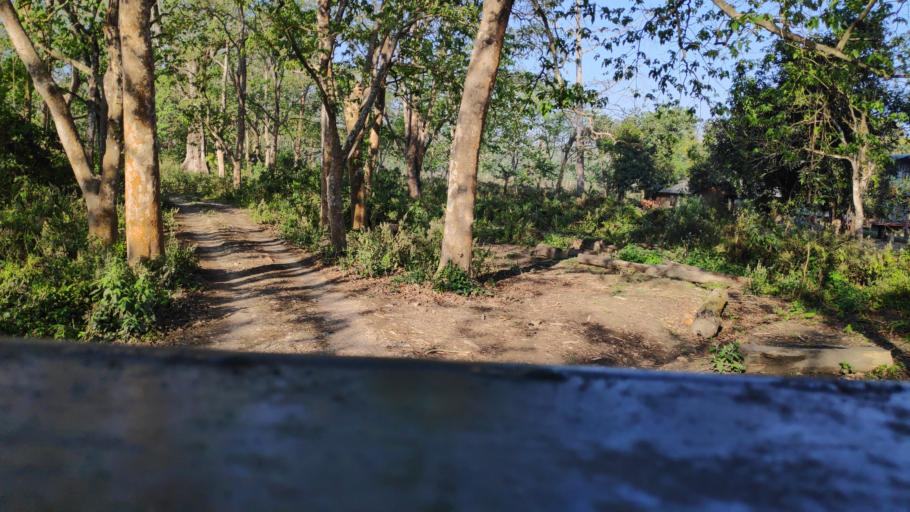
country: NP
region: Central Region
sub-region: Narayani Zone
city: Bharatpur
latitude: 27.5588
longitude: 84.5584
